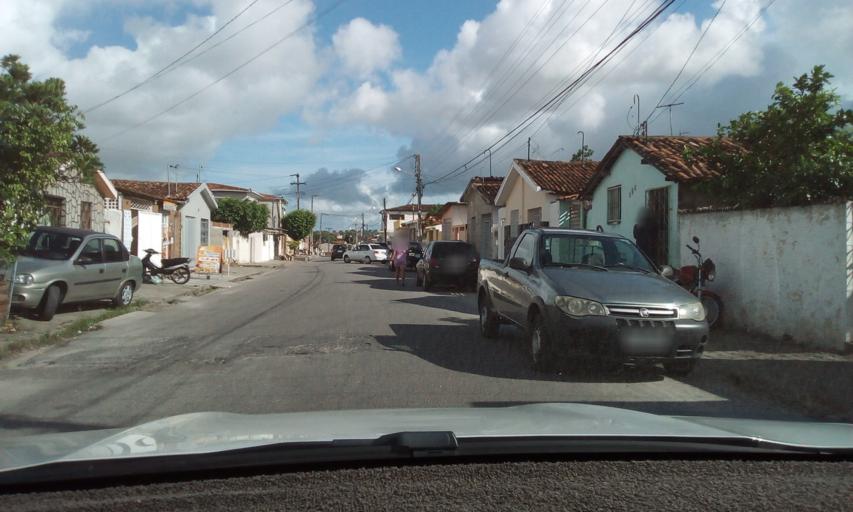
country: BR
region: Paraiba
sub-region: Bayeux
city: Bayeux
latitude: -7.1279
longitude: -34.9220
